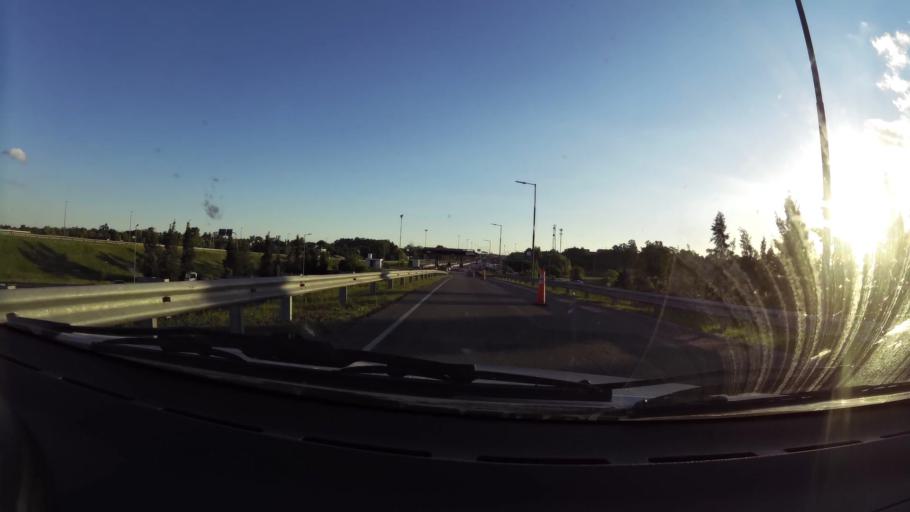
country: AR
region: Buenos Aires
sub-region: Partido de Quilmes
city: Quilmes
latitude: -34.7829
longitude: -58.1526
